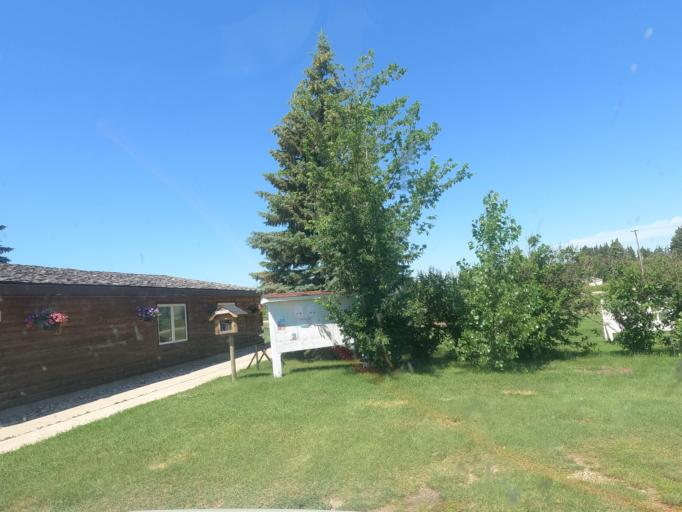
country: CA
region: Saskatchewan
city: Moosomin
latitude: 49.5766
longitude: -101.7044
